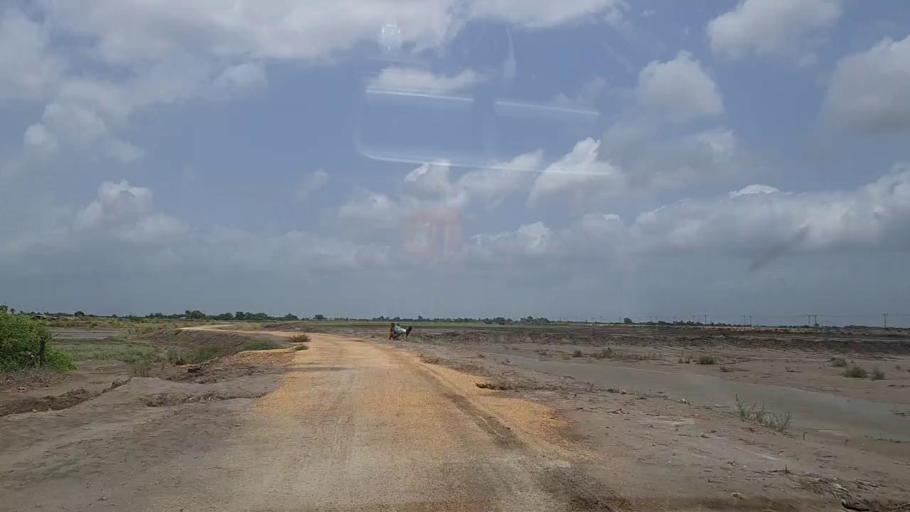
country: PK
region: Sindh
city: Thatta
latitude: 24.6214
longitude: 68.0358
